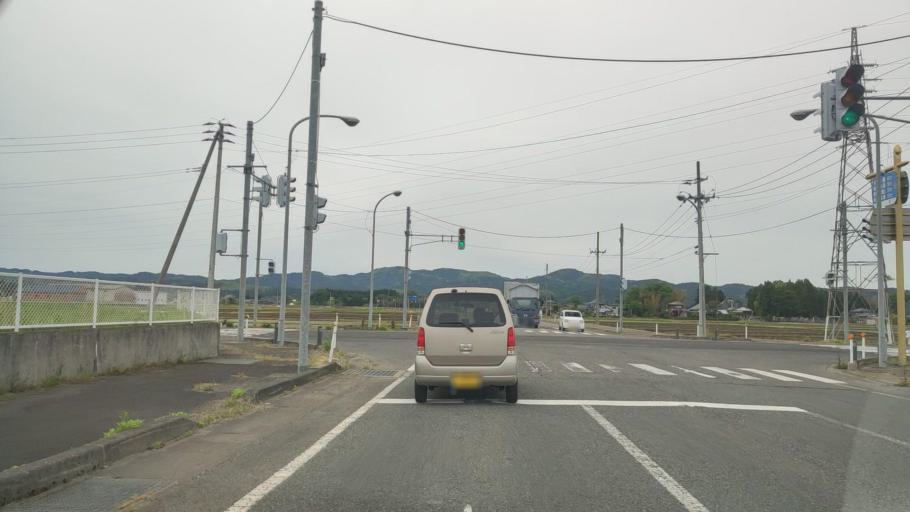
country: JP
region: Niigata
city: Gosen
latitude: 37.7293
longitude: 139.1665
